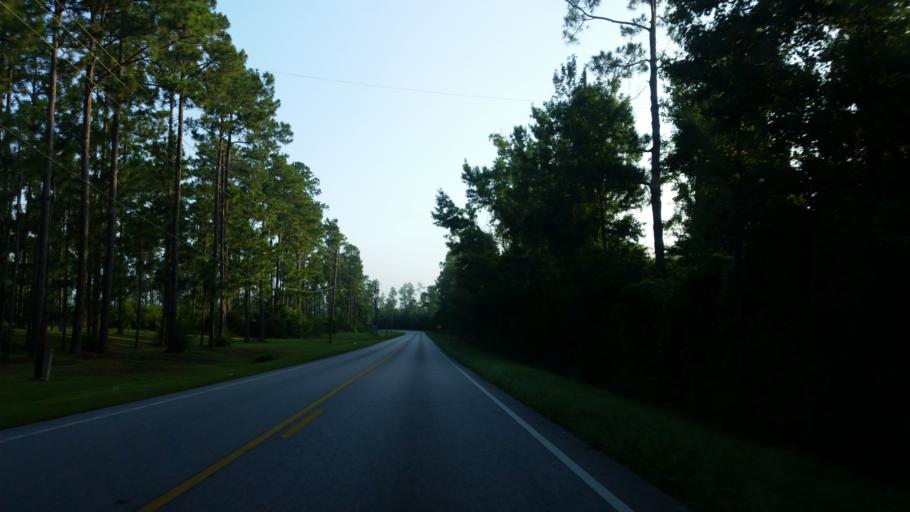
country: US
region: Florida
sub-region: Escambia County
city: Molino
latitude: 30.6740
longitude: -87.3194
